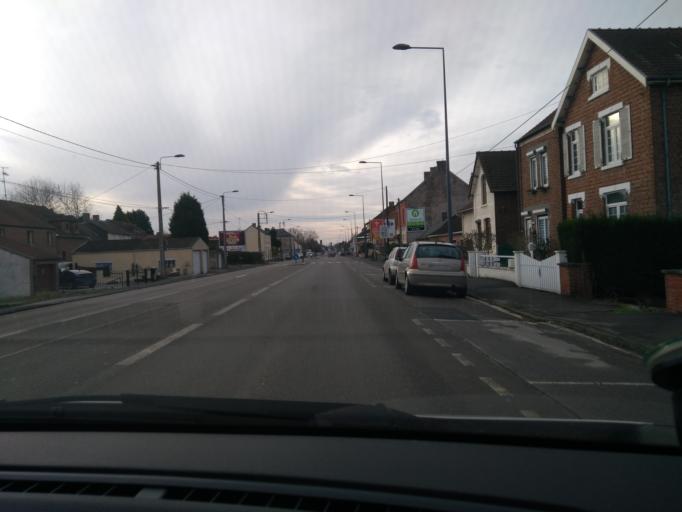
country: FR
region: Nord-Pas-de-Calais
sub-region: Departement du Nord
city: Maubeuge
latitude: 50.3001
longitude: 3.9773
